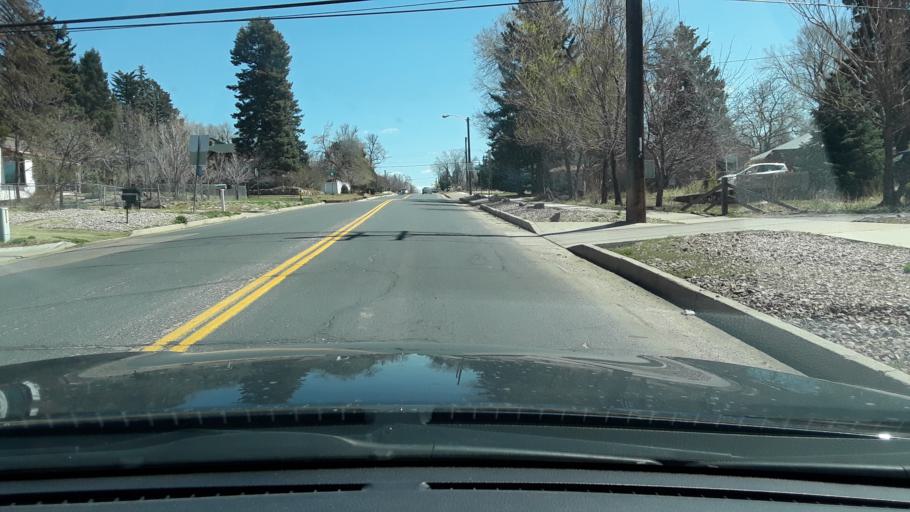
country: US
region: Colorado
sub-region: El Paso County
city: Colorado Springs
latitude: 38.8489
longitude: -104.7938
